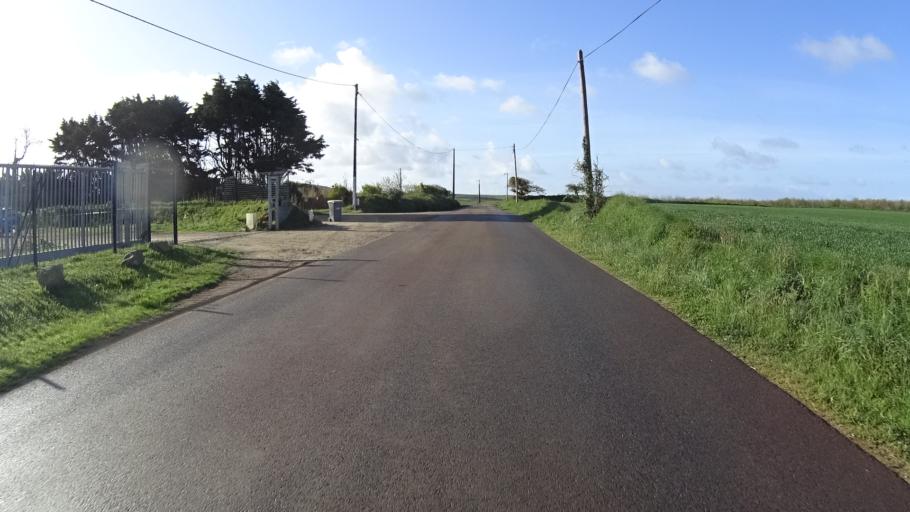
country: FR
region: Brittany
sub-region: Departement du Finistere
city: Plouarzel
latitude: 48.4311
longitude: -4.7148
